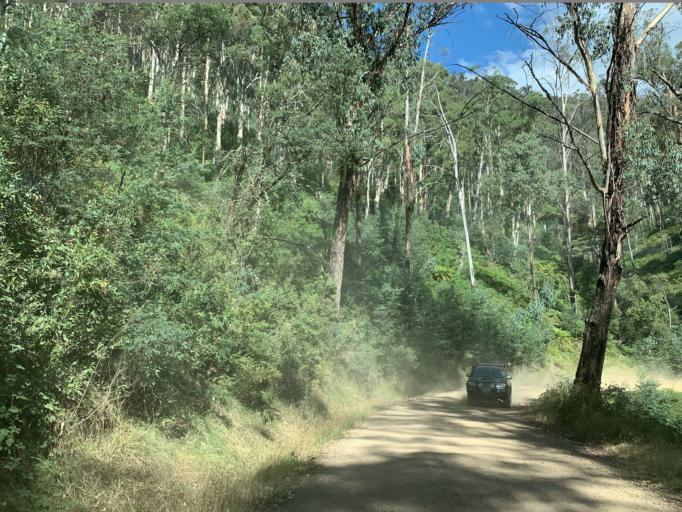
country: AU
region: Victoria
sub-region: Mansfield
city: Mansfield
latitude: -37.0936
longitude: 146.5277
